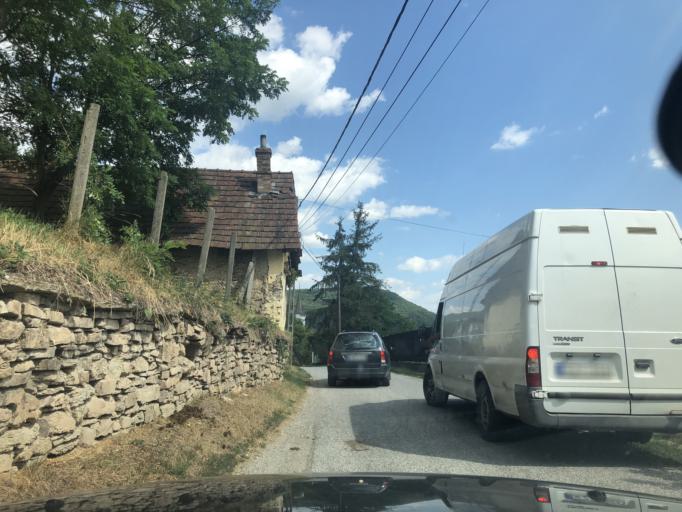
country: HU
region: Borsod-Abauj-Zemplen
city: Szendro
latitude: 48.4737
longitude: 20.6821
